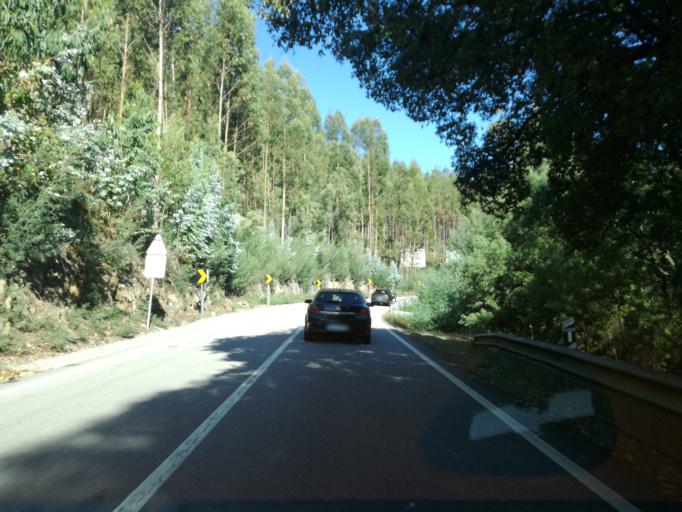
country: PT
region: Porto
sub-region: Pacos de Ferreira
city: Seroa
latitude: 41.2570
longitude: -8.4550
